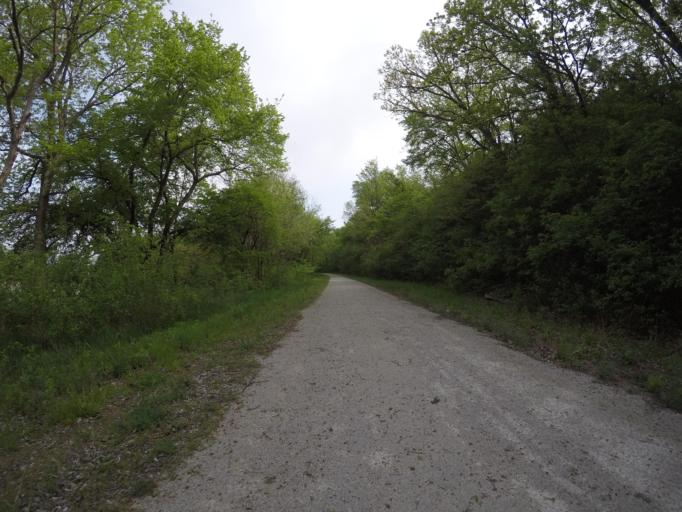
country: US
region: Kansas
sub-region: Marshall County
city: Marysville
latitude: 39.9699
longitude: -96.6000
